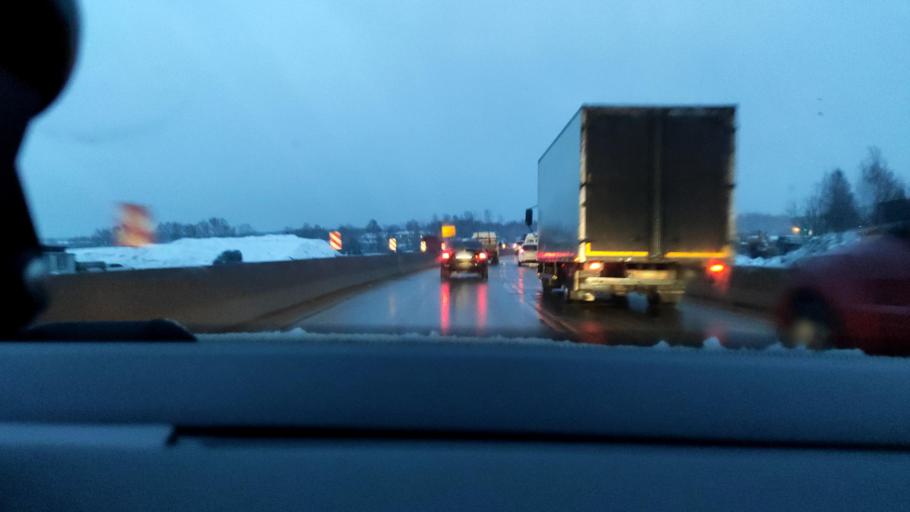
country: RU
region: Moskovskaya
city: Kubinka
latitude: 55.5690
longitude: 36.6968
